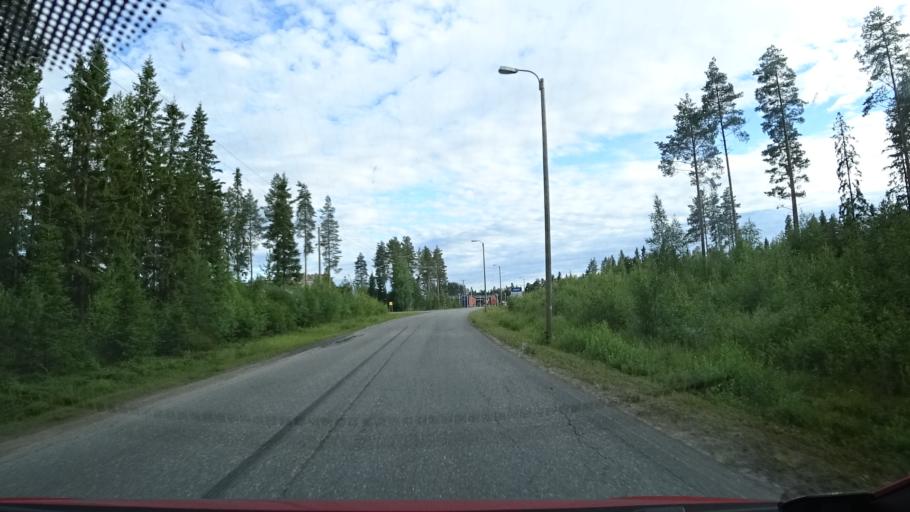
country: FI
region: Northern Ostrobothnia
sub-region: Oulu
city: Haukipudas
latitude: 65.1986
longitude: 25.4136
